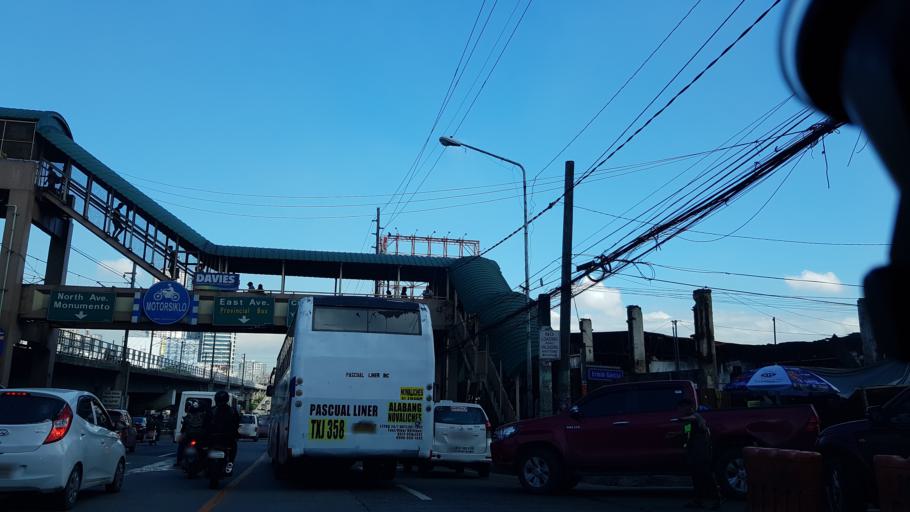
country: PH
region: Metro Manila
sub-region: Quezon City
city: Quezon City
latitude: 14.6273
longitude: 121.0476
